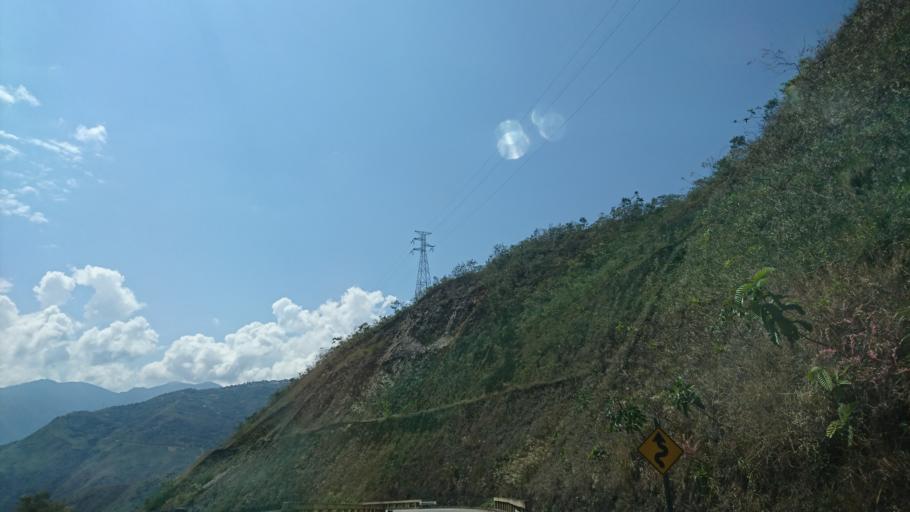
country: BO
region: La Paz
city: Coroico
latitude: -16.2024
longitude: -67.7613
